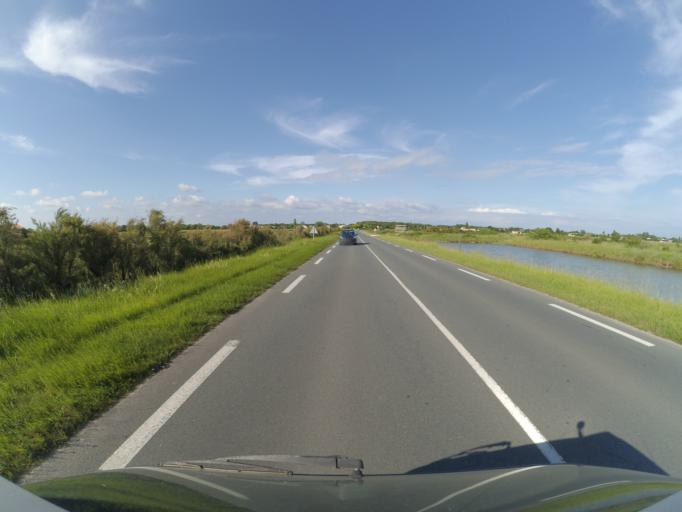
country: FR
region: Poitou-Charentes
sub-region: Departement de la Charente-Maritime
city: Saint-Sulpice-de-Royan
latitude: 45.6992
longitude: -0.9874
